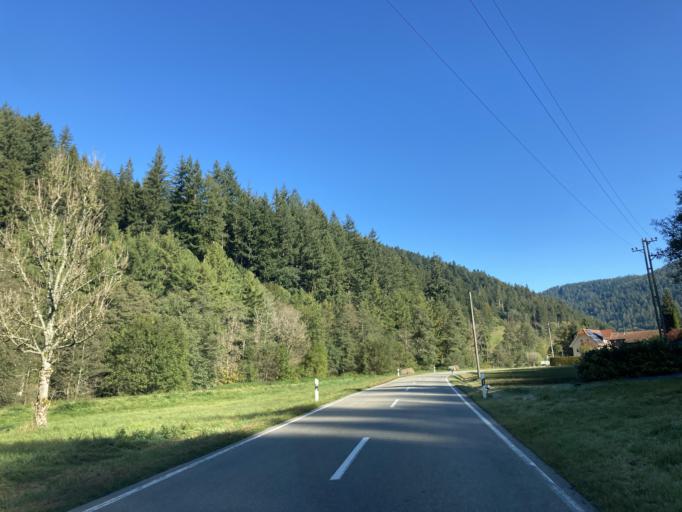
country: DE
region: Baden-Wuerttemberg
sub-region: Karlsruhe Region
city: Bad Rippoldsau-Schapbach
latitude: 48.4059
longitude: 8.3171
